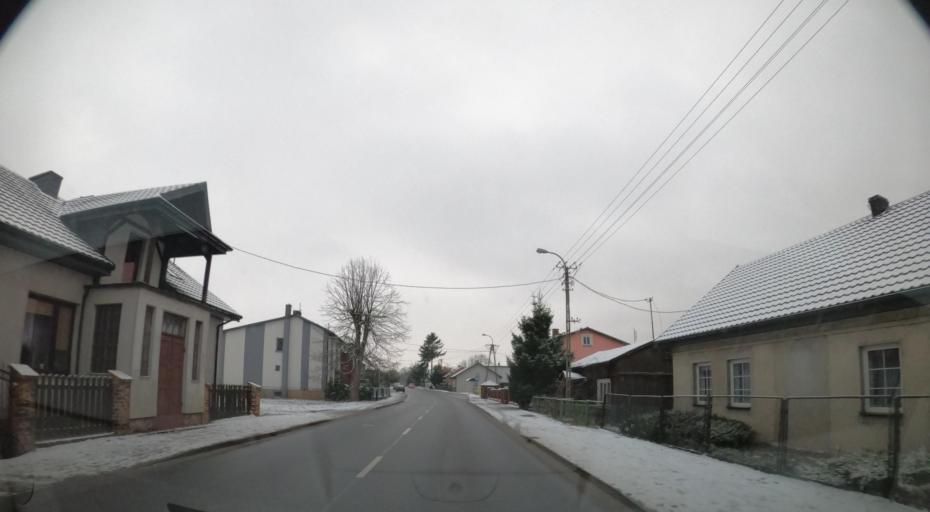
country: PL
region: Kujawsko-Pomorskie
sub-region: Powiat lipnowski
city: Wielgie
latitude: 52.7406
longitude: 19.2655
